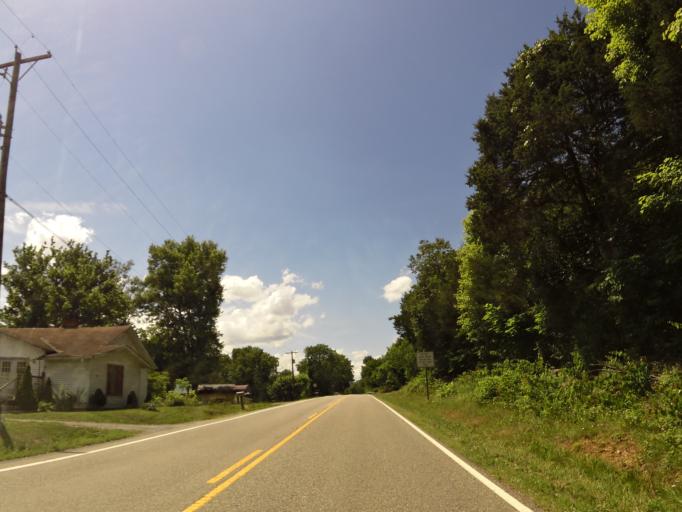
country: US
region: Virginia
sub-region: Lee County
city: Dryden
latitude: 36.7132
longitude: -82.9705
